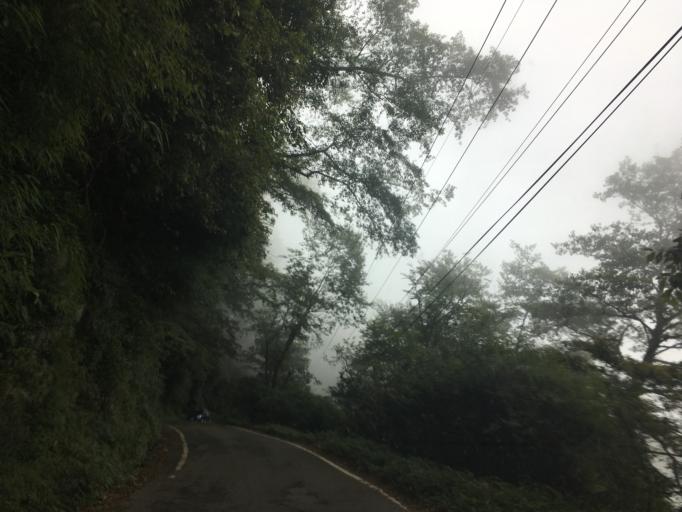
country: TW
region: Taiwan
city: Fengyuan
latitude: 24.2277
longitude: 120.9642
